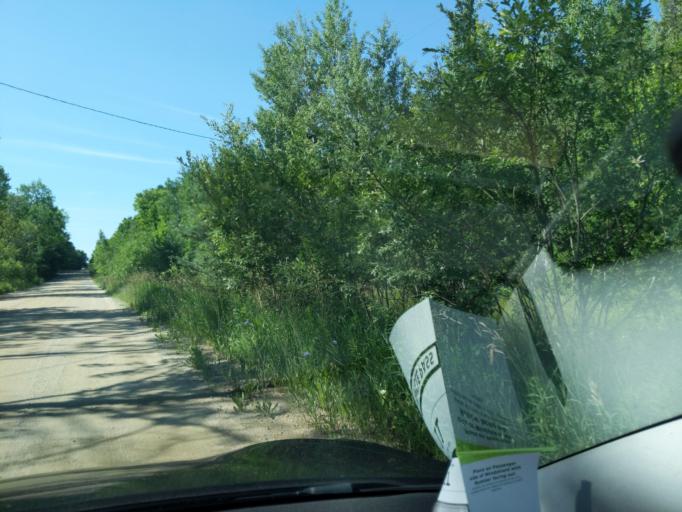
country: US
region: Michigan
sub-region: Cheboygan County
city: Cheboygan
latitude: 45.6746
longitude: -84.6508
